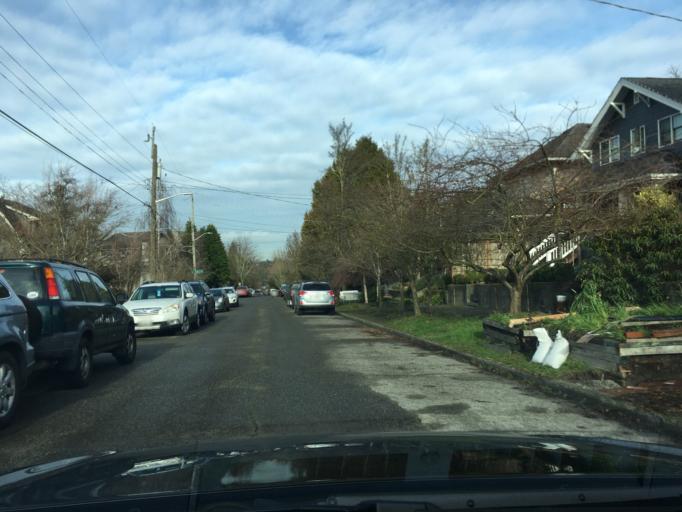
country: US
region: Washington
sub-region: King County
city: Seattle
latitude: 47.6675
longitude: -122.3322
